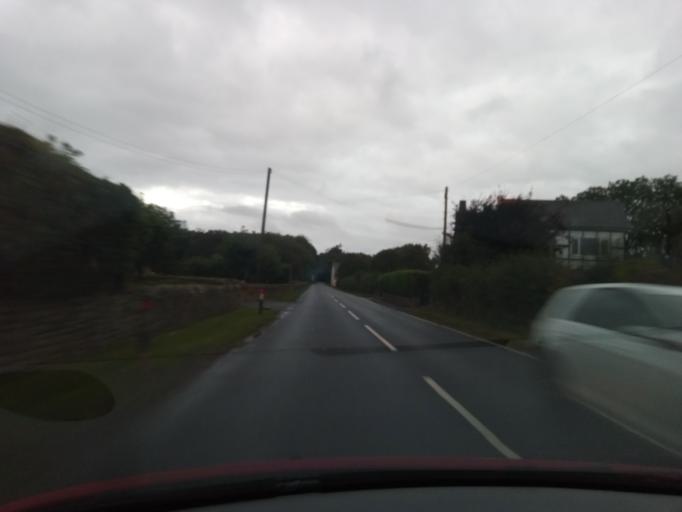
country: GB
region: England
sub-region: Darlington
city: High Coniscliffe
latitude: 54.5401
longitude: -1.6732
